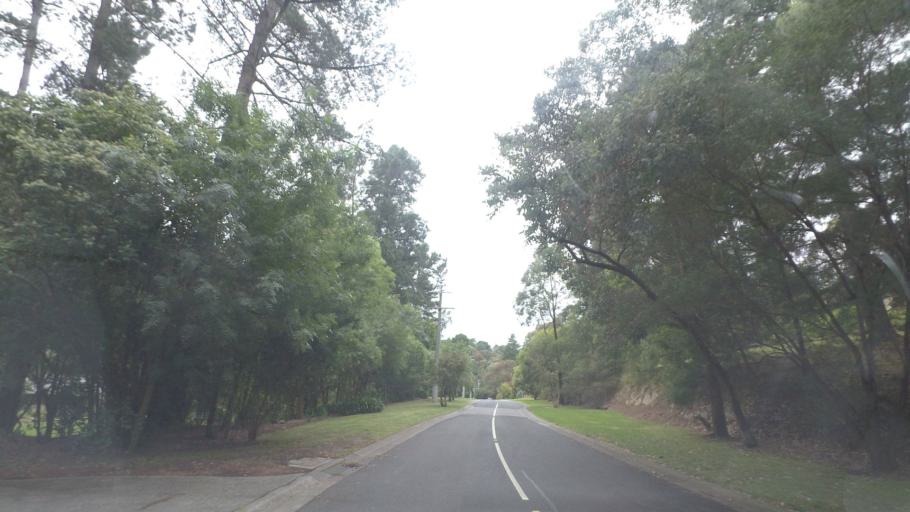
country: AU
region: Victoria
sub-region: Manningham
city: Park Orchards
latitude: -37.7867
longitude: 145.2126
